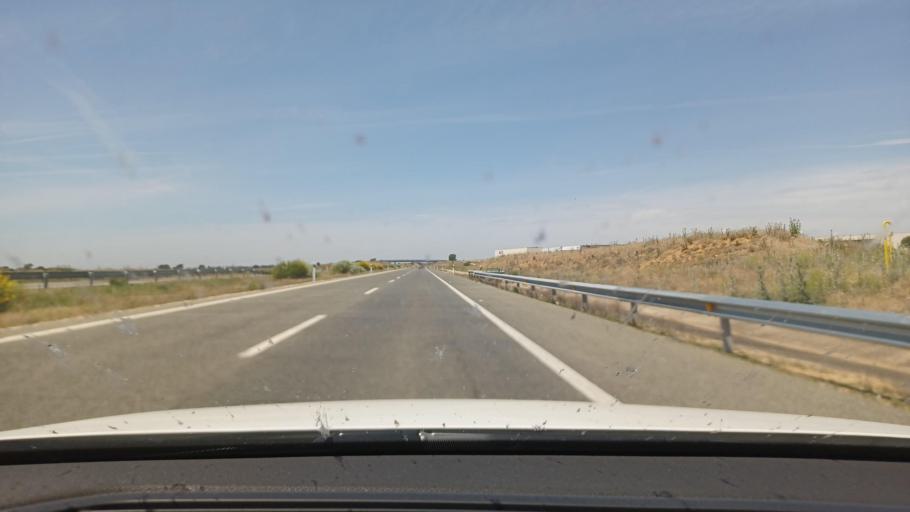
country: ES
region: Madrid
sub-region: Provincia de Madrid
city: Camarma de Esteruelas
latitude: 40.5244
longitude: -3.3818
